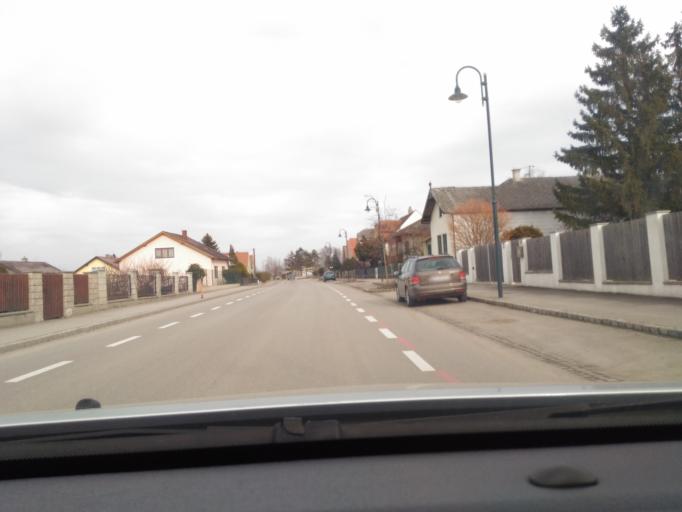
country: AT
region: Lower Austria
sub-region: Politischer Bezirk Hollabrunn
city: Zellerndorf
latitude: 48.6985
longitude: 15.9713
